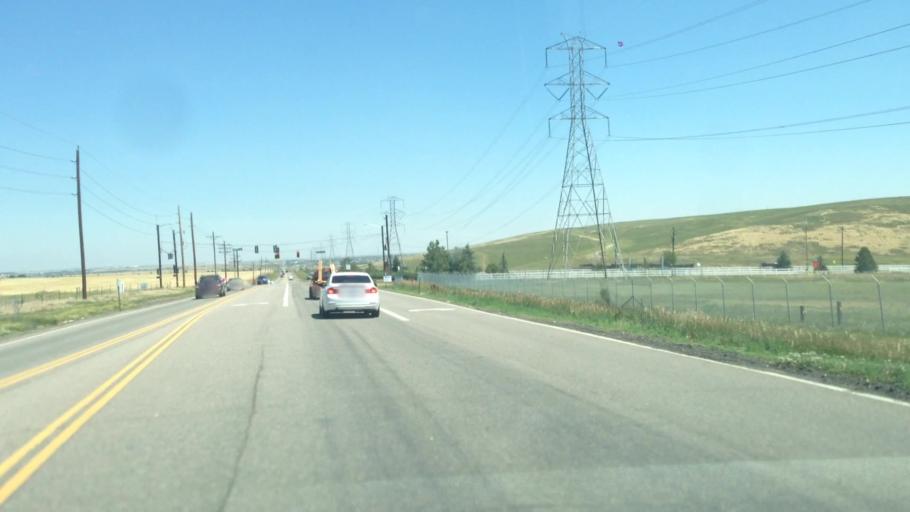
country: US
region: Colorado
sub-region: Arapahoe County
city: Dove Valley
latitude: 39.6513
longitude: -104.7162
